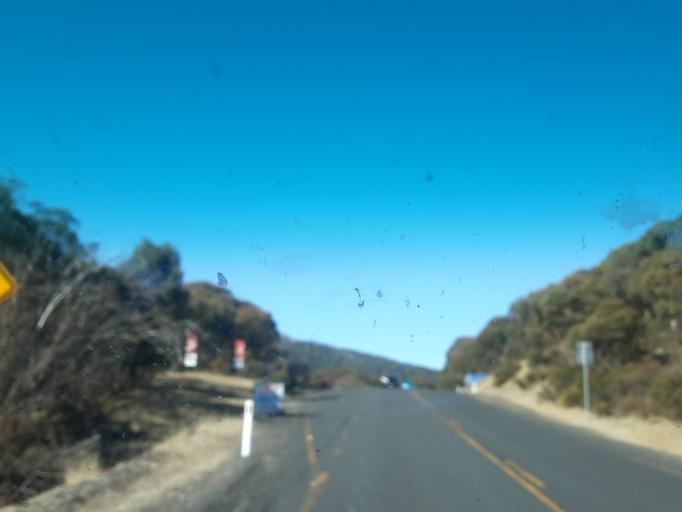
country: AU
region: New South Wales
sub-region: Snowy River
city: Jindabyne
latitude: -36.4501
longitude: 148.4497
